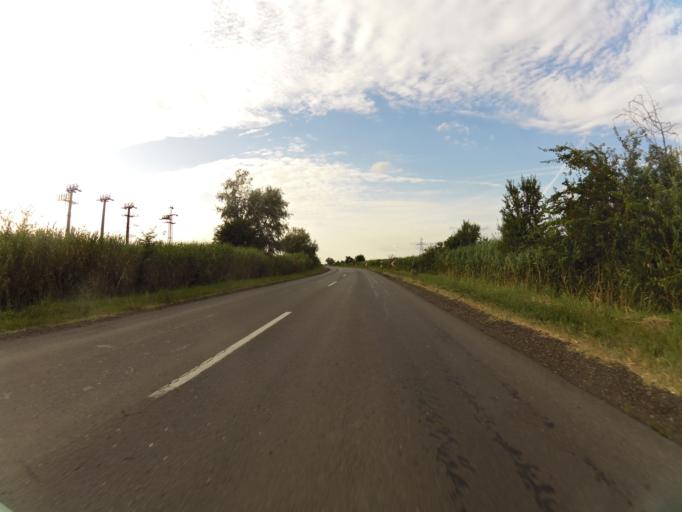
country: HU
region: Csongrad
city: Szeged
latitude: 46.3080
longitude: 20.1307
